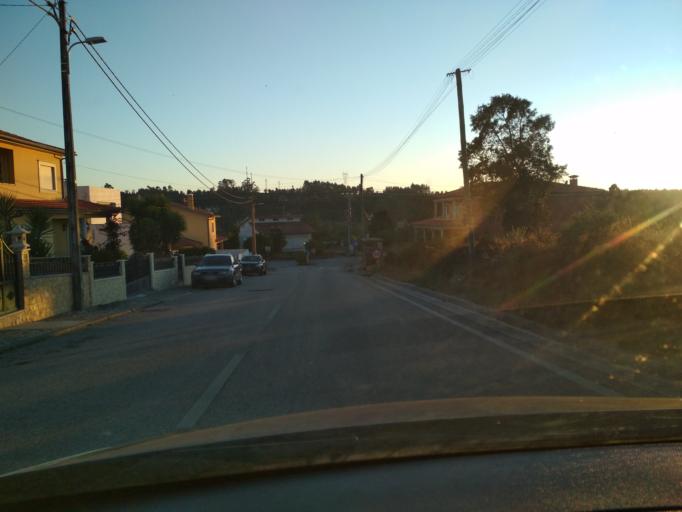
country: PT
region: Coimbra
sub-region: Condeixa-A-Nova
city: Condeixa-a-Nova
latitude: 40.1761
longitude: -8.4834
